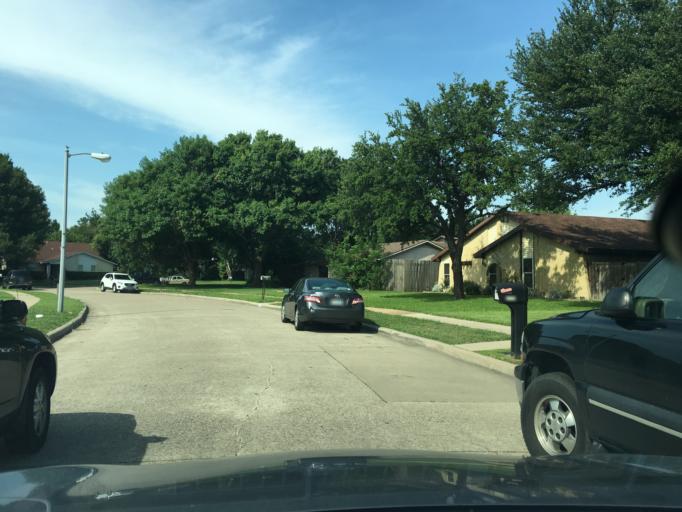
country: US
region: Texas
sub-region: Dallas County
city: Richardson
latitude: 32.9652
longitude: -96.6840
